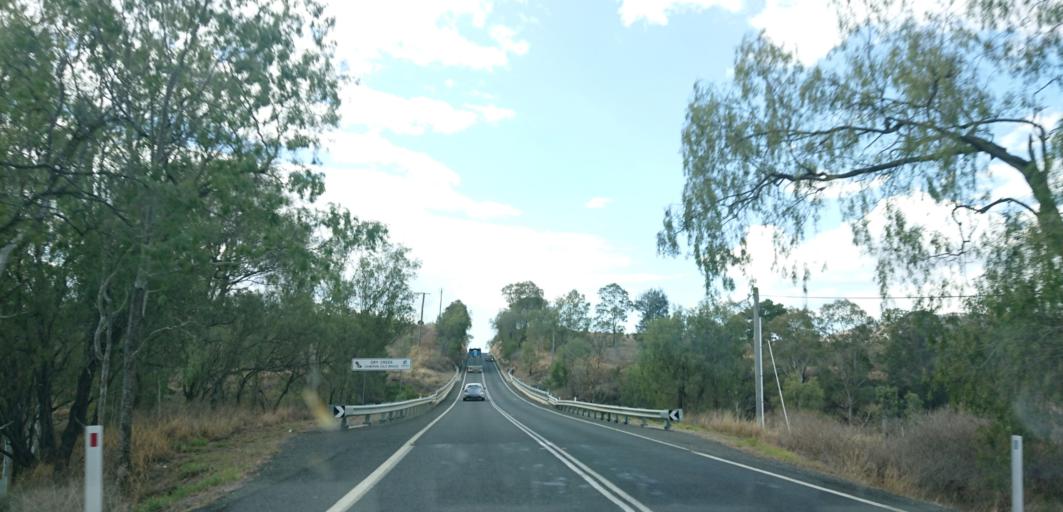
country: AU
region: Queensland
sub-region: Lockyer Valley
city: Gatton
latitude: -27.6608
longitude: 152.1632
